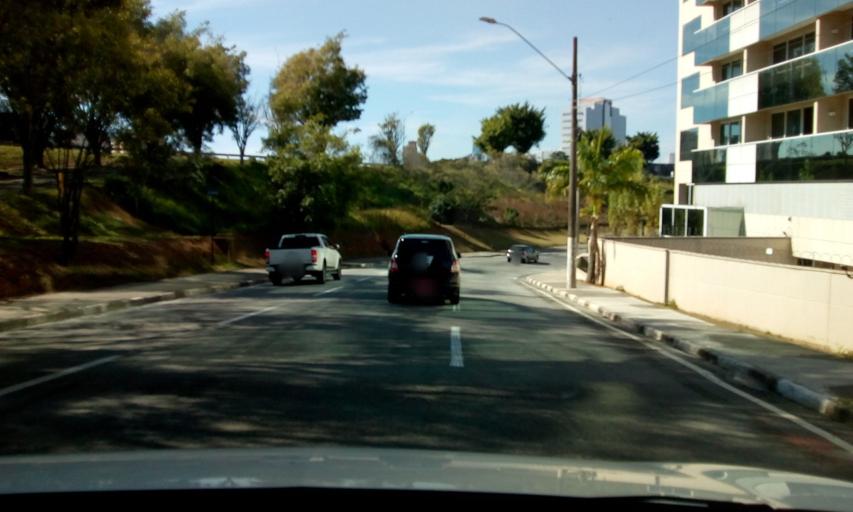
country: BR
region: Sao Paulo
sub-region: Barueri
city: Barueri
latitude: -23.5057
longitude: -46.8700
